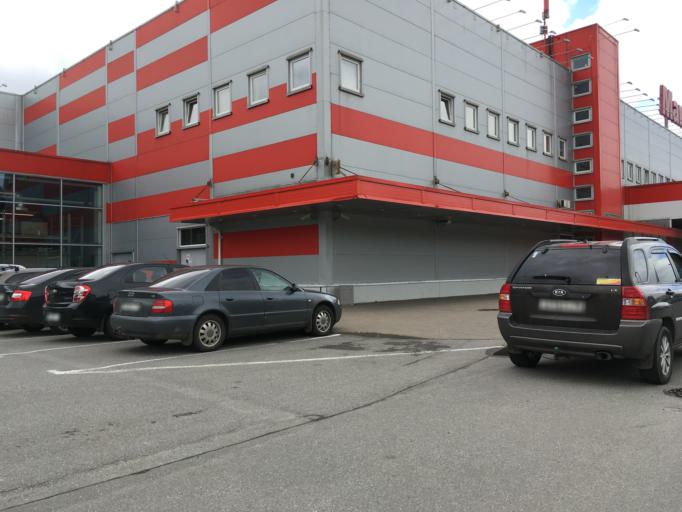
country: RU
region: St.-Petersburg
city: Obukhovo
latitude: 59.8920
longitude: 30.4772
